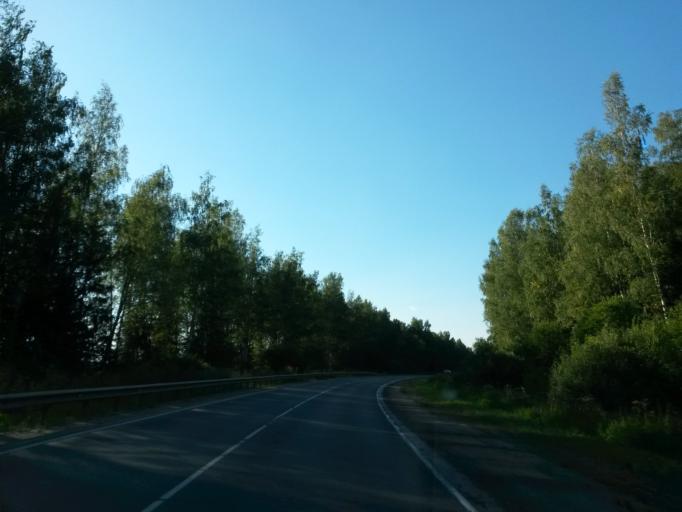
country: RU
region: Ivanovo
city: Pistsovo
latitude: 57.0784
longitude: 40.6769
